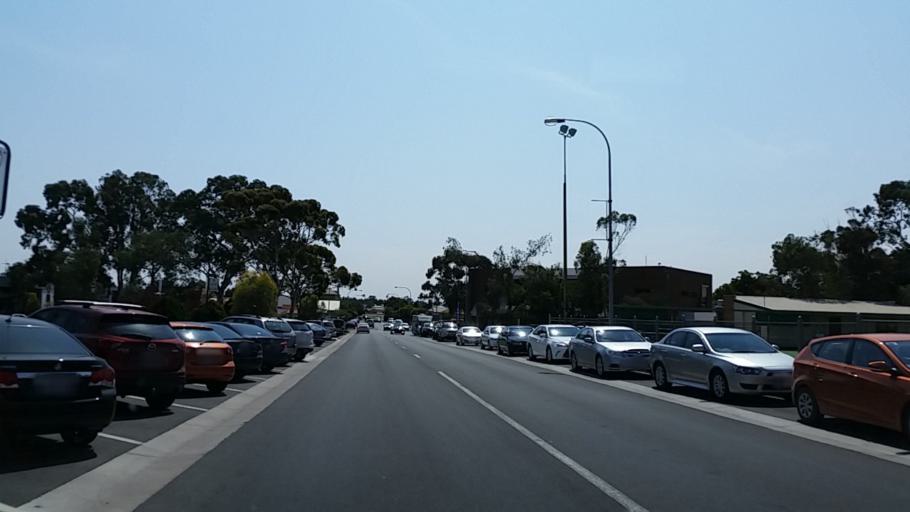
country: AU
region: South Australia
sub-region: Port Augusta
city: Port Augusta West
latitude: -32.4917
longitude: 137.7643
